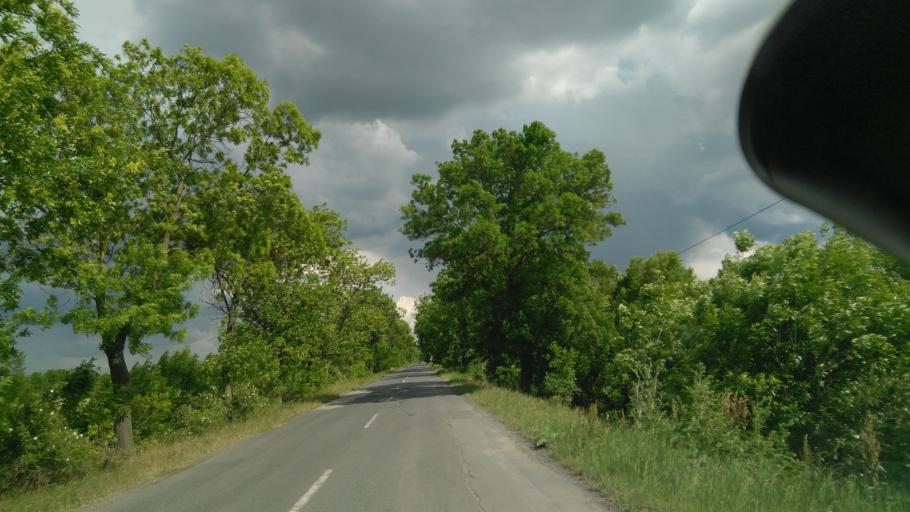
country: HU
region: Bekes
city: Bucsa
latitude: 47.1975
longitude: 21.0112
